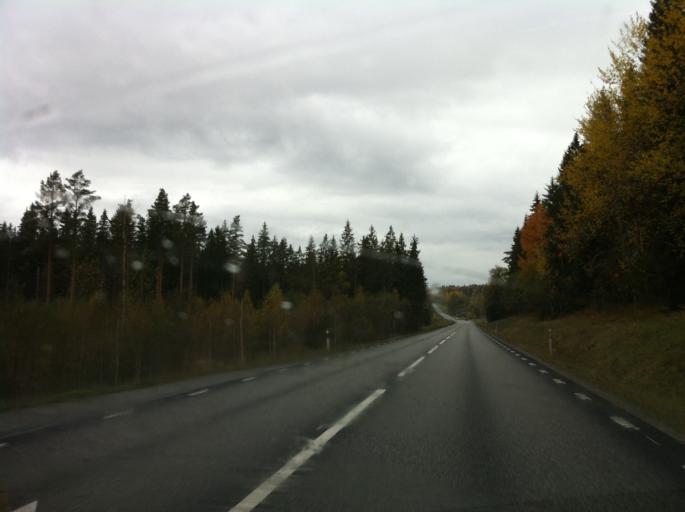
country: SE
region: OErebro
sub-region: Lindesbergs Kommun
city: Stora
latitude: 59.6743
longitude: 15.1002
